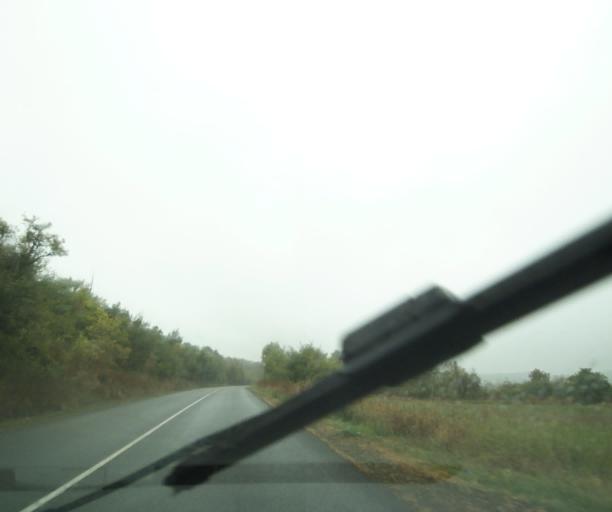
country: FR
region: Auvergne
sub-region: Departement du Puy-de-Dome
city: Chateaugay
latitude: 45.8432
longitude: 3.0825
